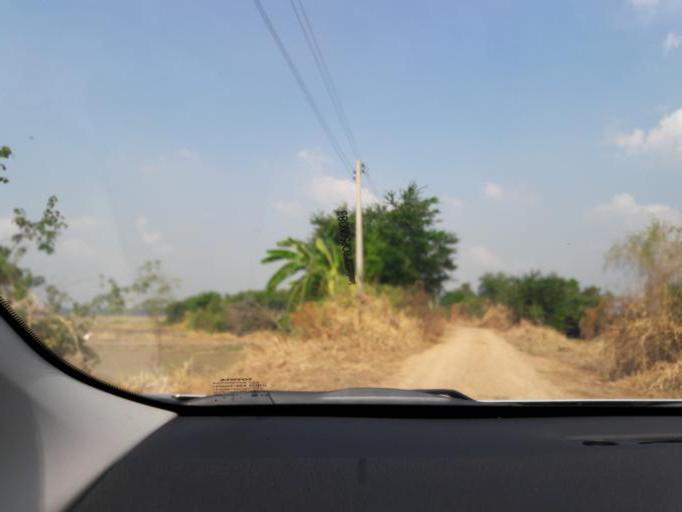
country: TH
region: Ang Thong
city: Ang Thong
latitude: 14.5639
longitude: 100.4100
